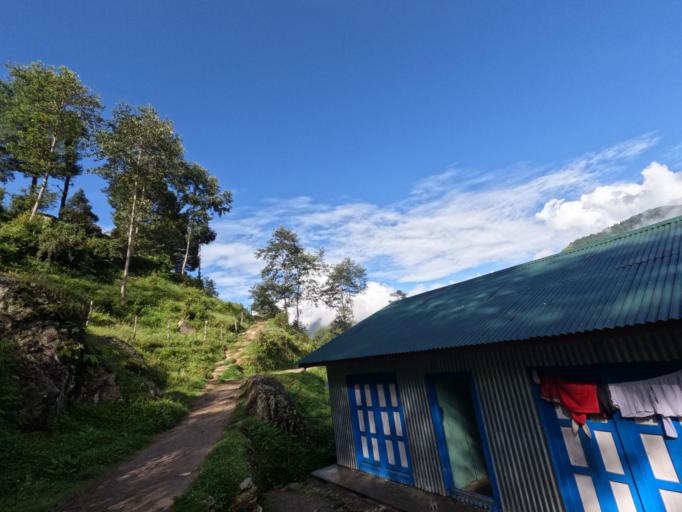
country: NP
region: Eastern Region
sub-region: Sagarmatha Zone
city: Namche Bazar
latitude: 27.4956
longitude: 86.5844
